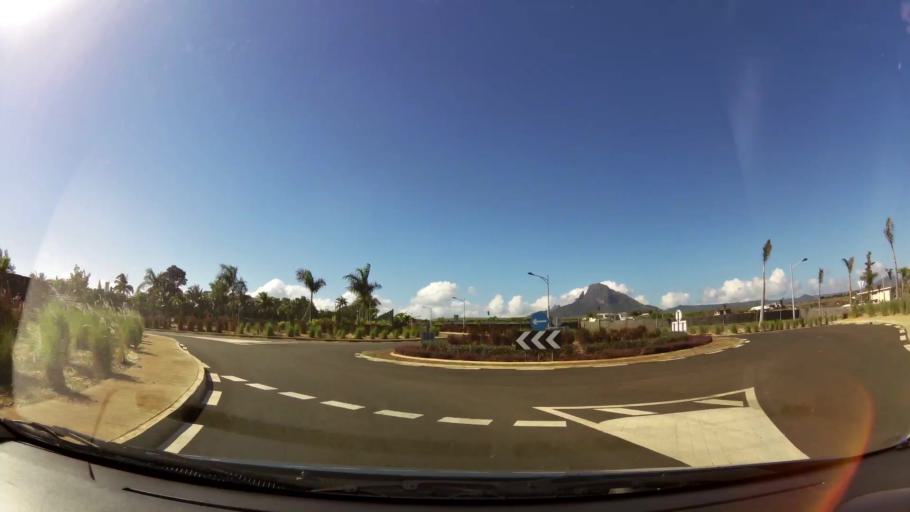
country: MU
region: Black River
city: Flic en Flac
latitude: -20.2671
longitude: 57.3820
